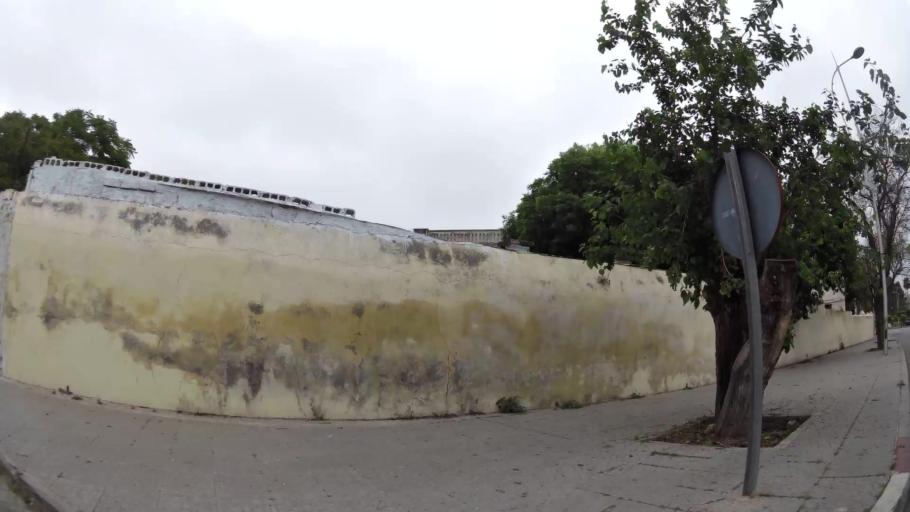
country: MA
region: Fes-Boulemane
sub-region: Fes
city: Fes
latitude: 34.0290
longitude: -4.9984
